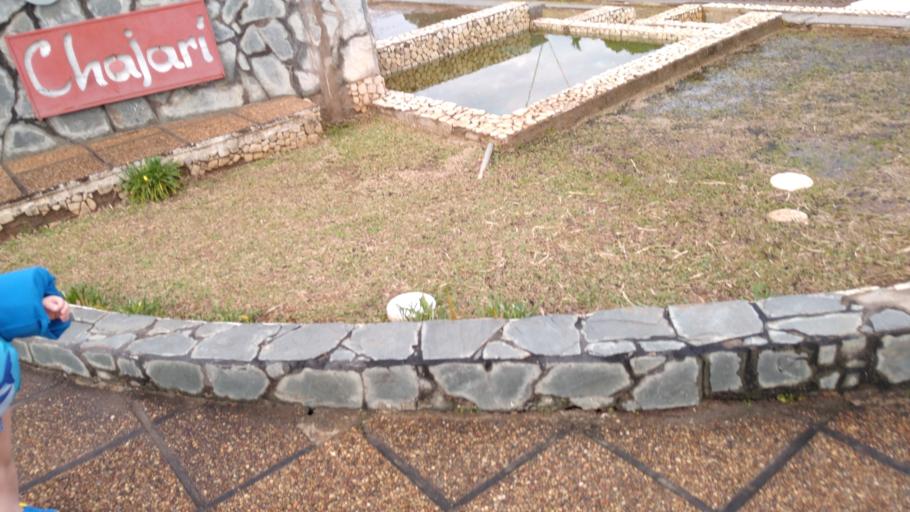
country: AR
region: Entre Rios
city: Chajari
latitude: -30.7457
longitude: -58.0138
